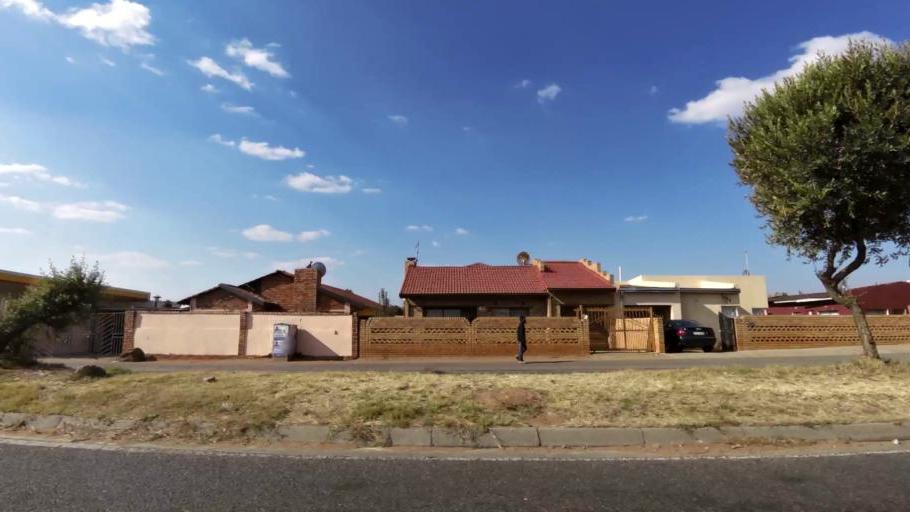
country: ZA
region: Gauteng
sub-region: City of Johannesburg Metropolitan Municipality
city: Soweto
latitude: -26.2227
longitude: 27.8724
